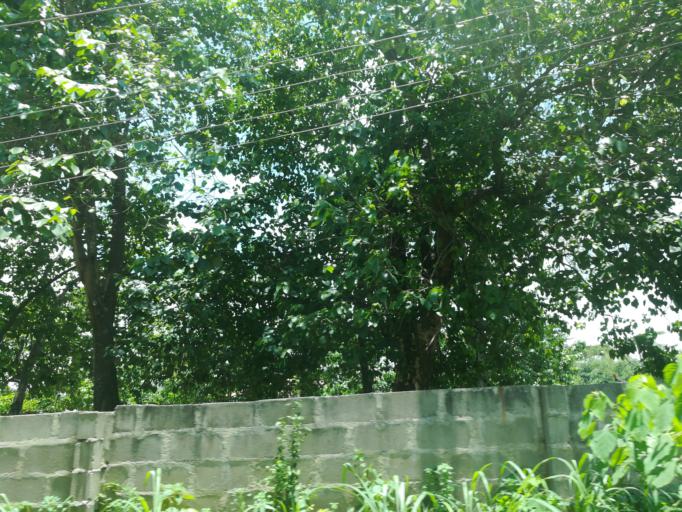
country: NG
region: Lagos
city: Ebute Ikorodu
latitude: 6.6043
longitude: 3.4947
